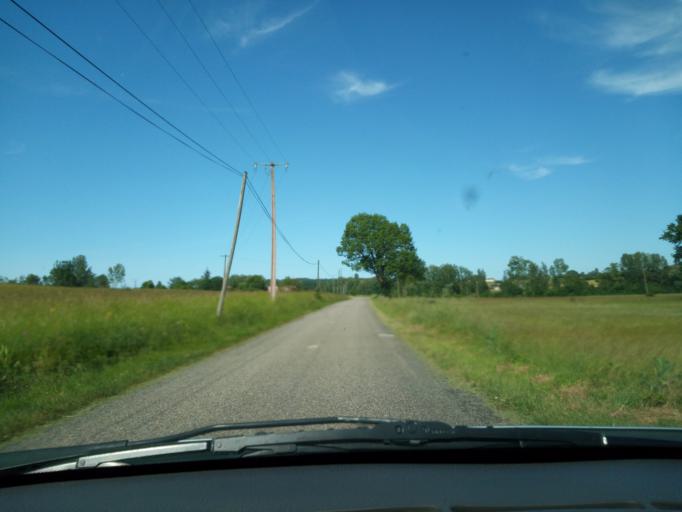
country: FR
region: Midi-Pyrenees
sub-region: Departement du Tarn-et-Garonne
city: Molieres
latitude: 44.2161
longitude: 1.3214
